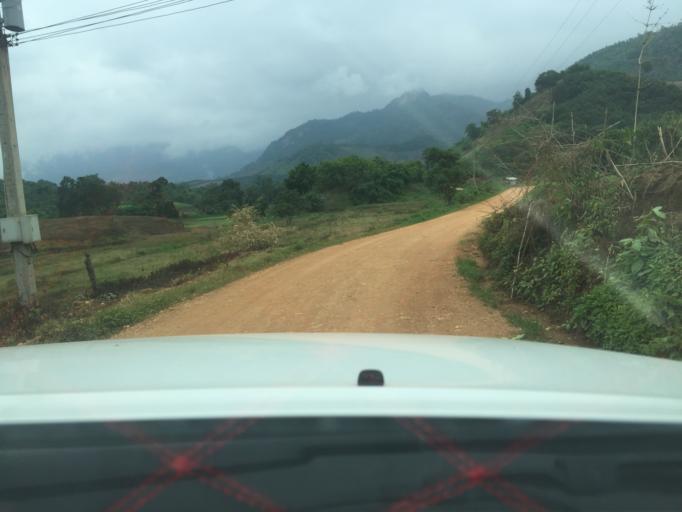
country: TH
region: Phayao
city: Phu Sang
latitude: 19.7313
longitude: 100.4801
